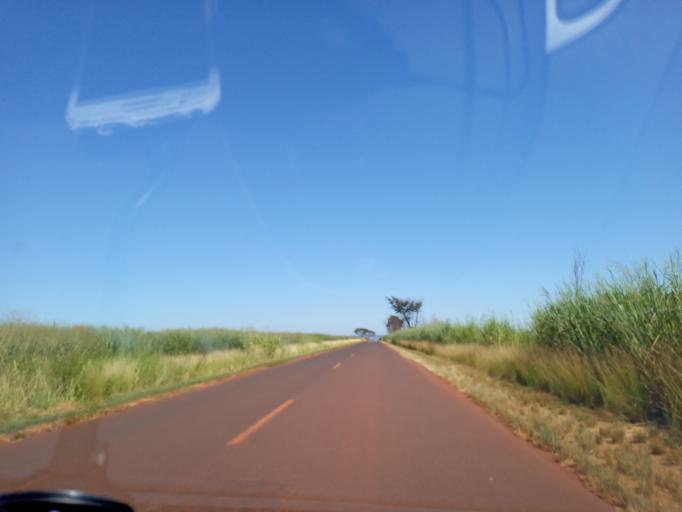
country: BR
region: Goias
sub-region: Itumbiara
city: Itumbiara
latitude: -18.4555
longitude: -49.1499
